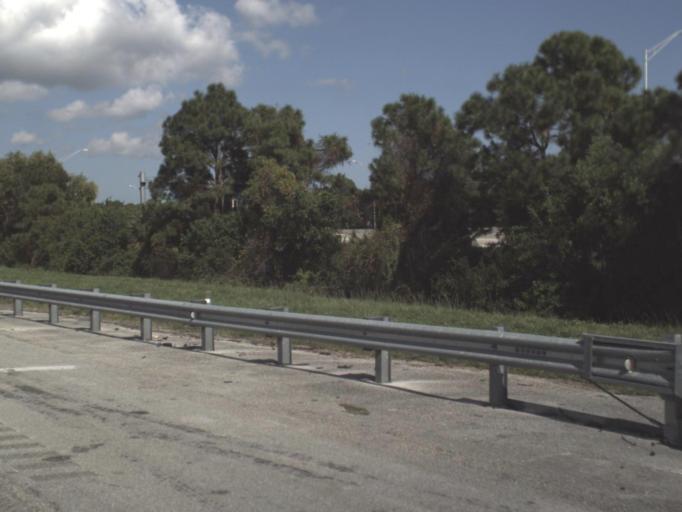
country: US
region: Florida
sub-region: Palm Beach County
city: Limestone Creek
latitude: 26.9143
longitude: -80.1447
